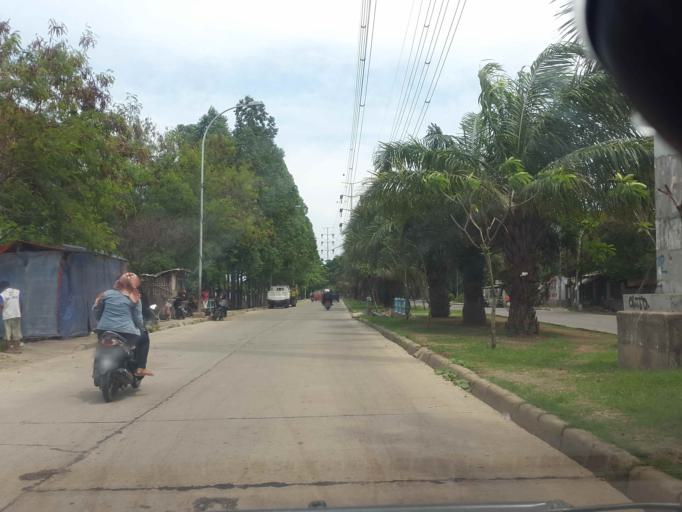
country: ID
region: Banten
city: Tangerang
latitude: -6.1547
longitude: 106.6460
